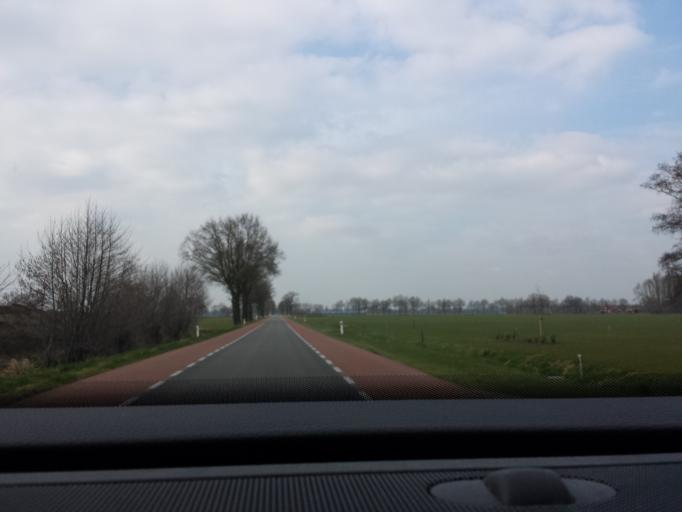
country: NL
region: Gelderland
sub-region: Oost Gelre
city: Lichtenvoorde
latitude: 52.0303
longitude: 6.4893
